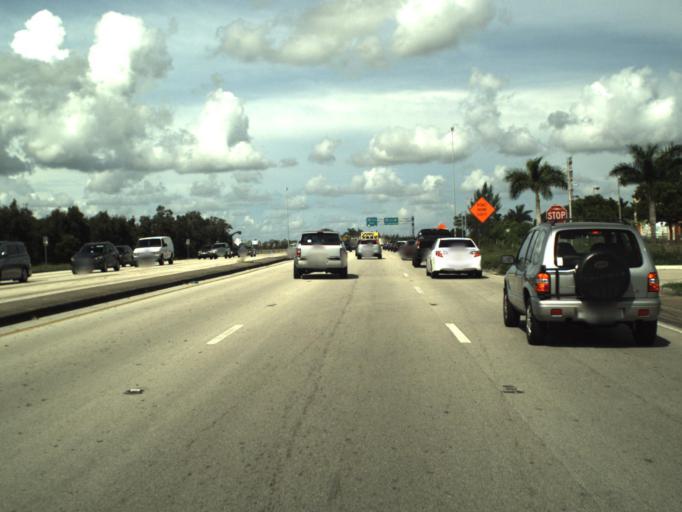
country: US
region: Florida
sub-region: Miami-Dade County
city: Palm Springs North
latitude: 25.9424
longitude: -80.3426
